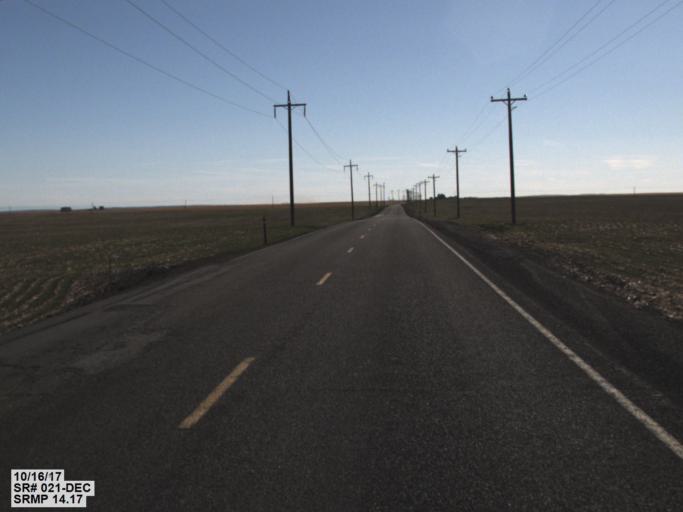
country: US
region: Washington
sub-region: Adams County
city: Ritzville
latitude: 46.8314
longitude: -118.5467
